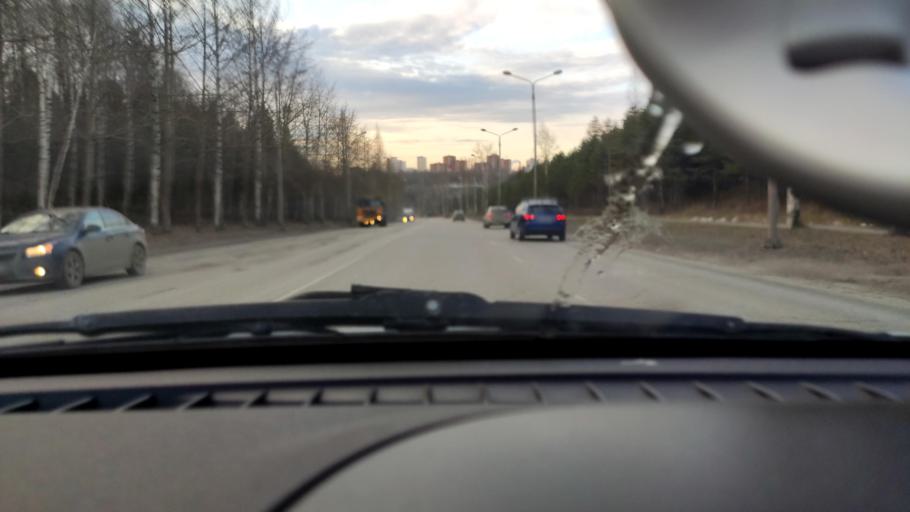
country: RU
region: Perm
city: Perm
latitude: 58.0764
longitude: 56.3702
